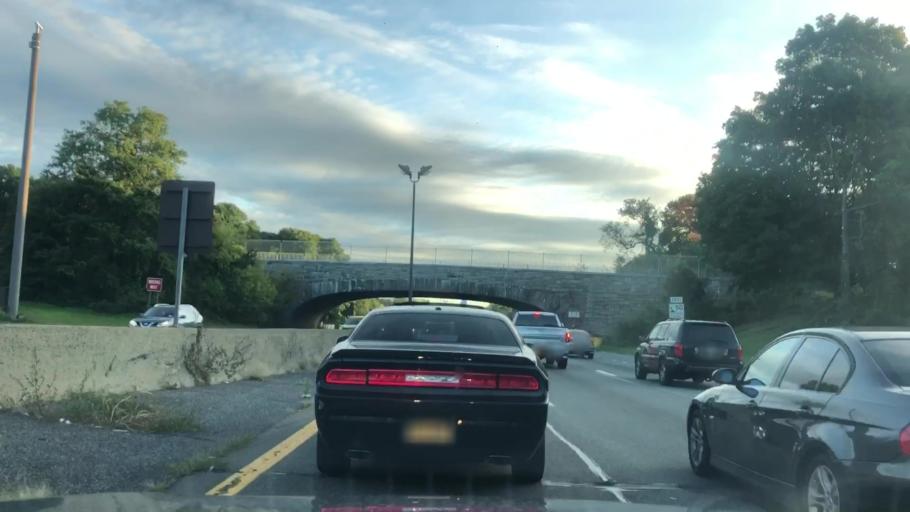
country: US
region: New York
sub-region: Nassau County
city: Lakeview
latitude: 40.6843
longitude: -73.6433
